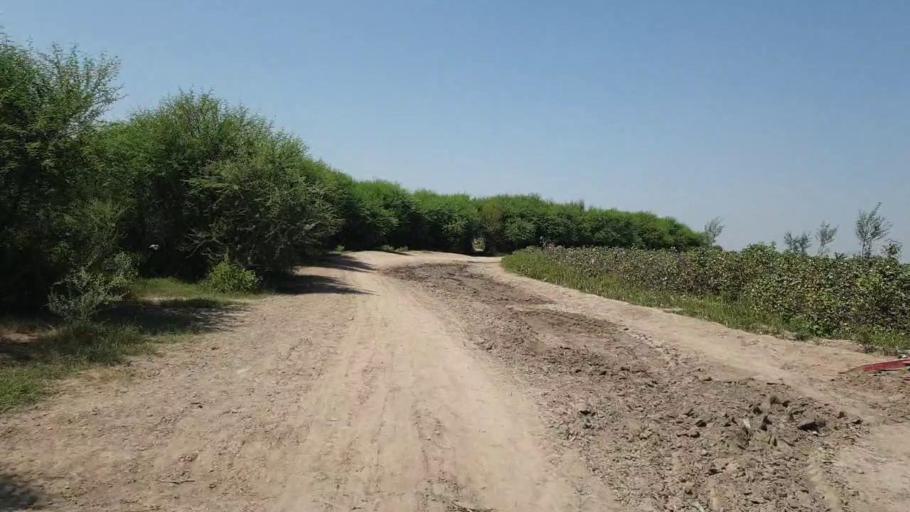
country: PK
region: Sindh
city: Hyderabad
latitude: 25.4669
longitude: 68.4251
